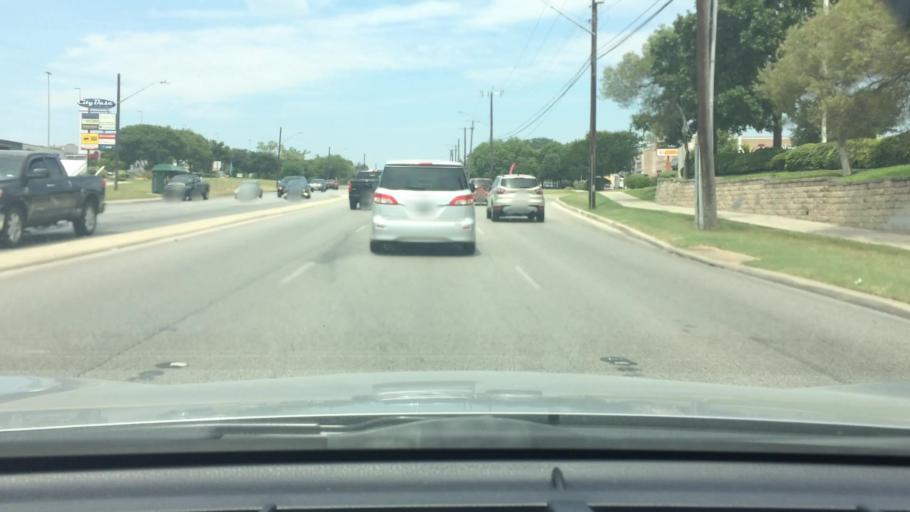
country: US
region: Texas
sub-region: Bexar County
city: San Antonio
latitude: 29.3518
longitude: -98.4352
